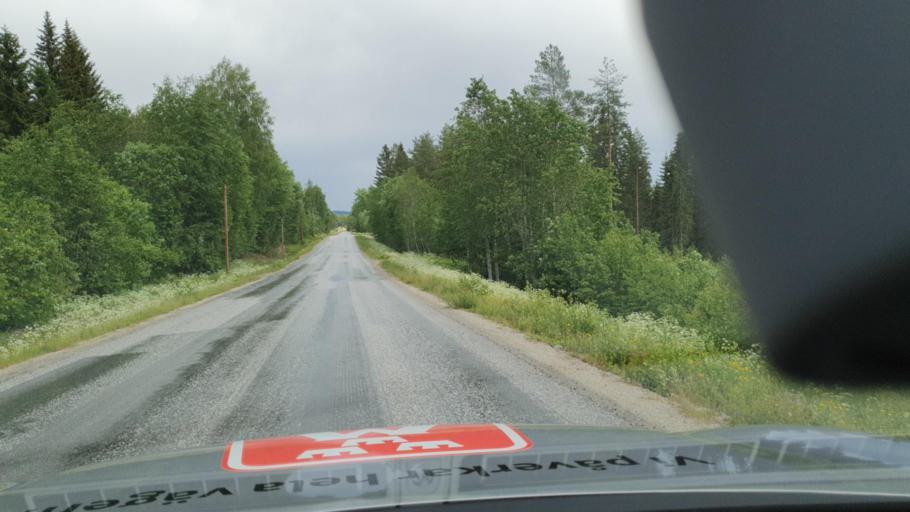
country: SE
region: Vaesternorrland
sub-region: OErnskoeldsviks Kommun
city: Bredbyn
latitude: 63.3315
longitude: 18.0478
